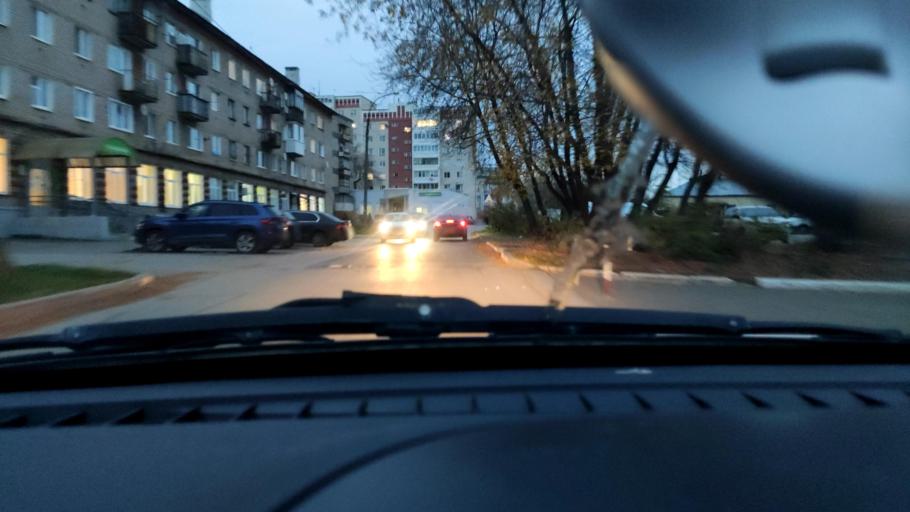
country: RU
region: Perm
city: Kondratovo
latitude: 58.0363
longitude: 56.1292
